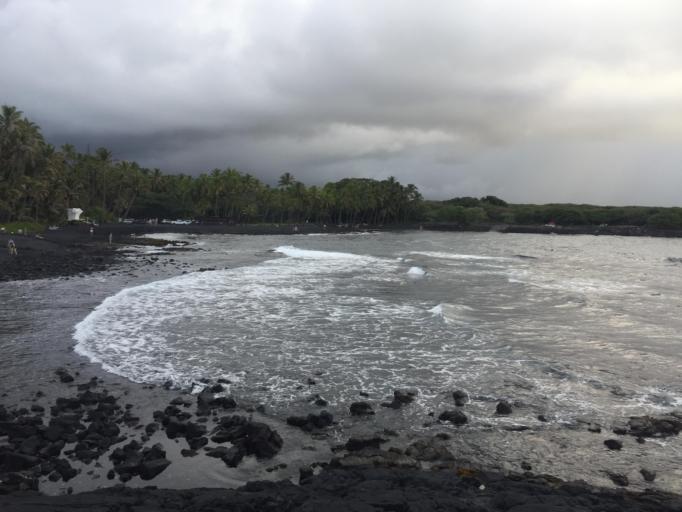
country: US
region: Hawaii
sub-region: Hawaii County
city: Pahala
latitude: 19.1344
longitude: -155.5050
